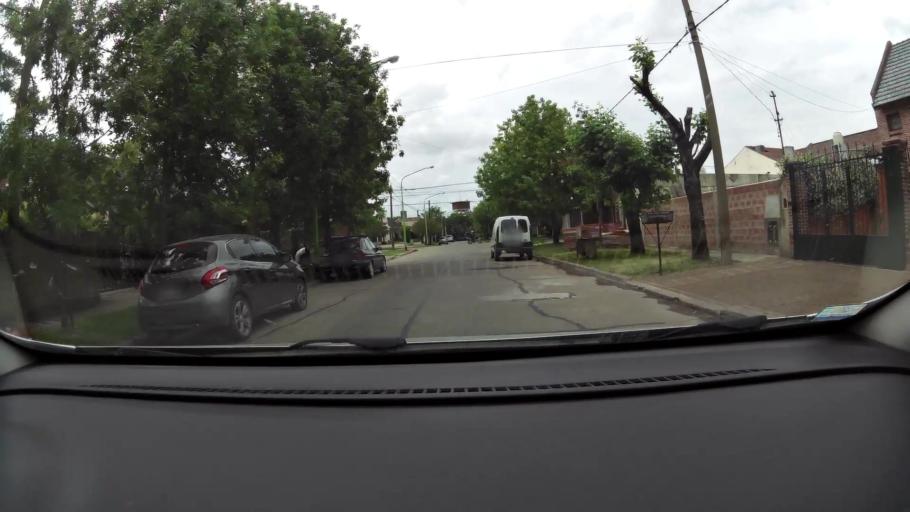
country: AR
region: Buenos Aires
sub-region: Partido de Campana
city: Campana
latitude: -34.1639
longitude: -58.9718
